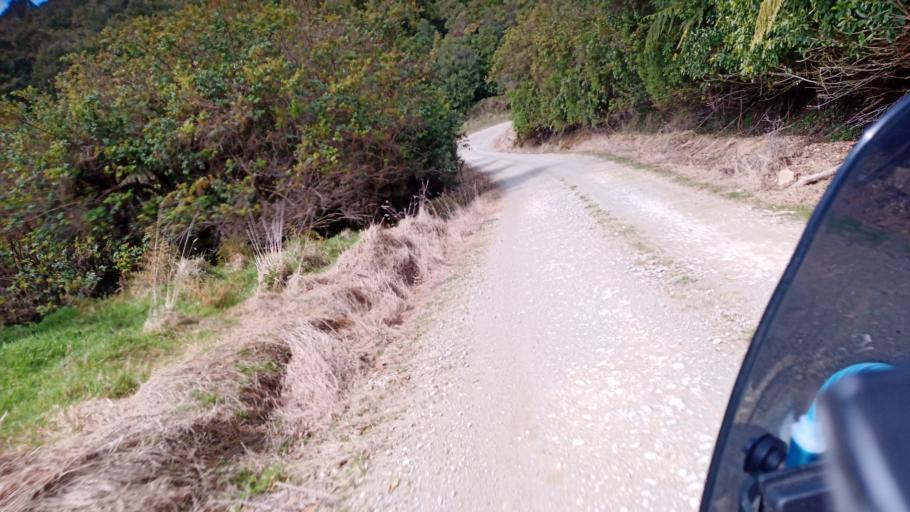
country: NZ
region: Gisborne
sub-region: Gisborne District
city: Gisborne
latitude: -38.8508
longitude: 177.7897
